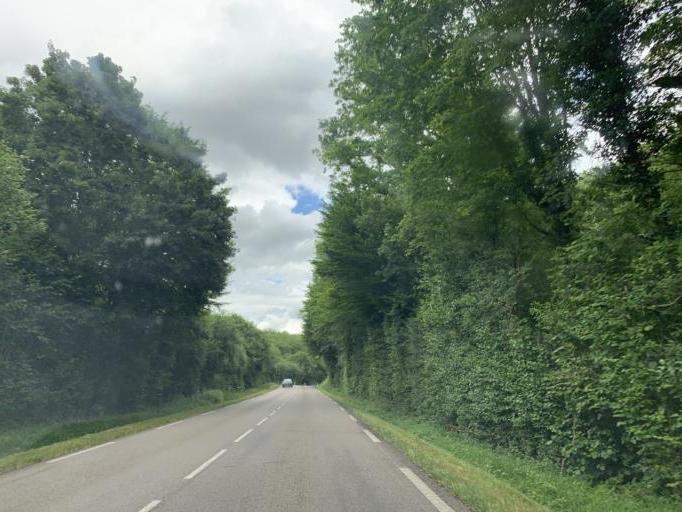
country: FR
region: Bourgogne
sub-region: Departement de l'Yonne
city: Chablis
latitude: 47.7380
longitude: 3.8121
